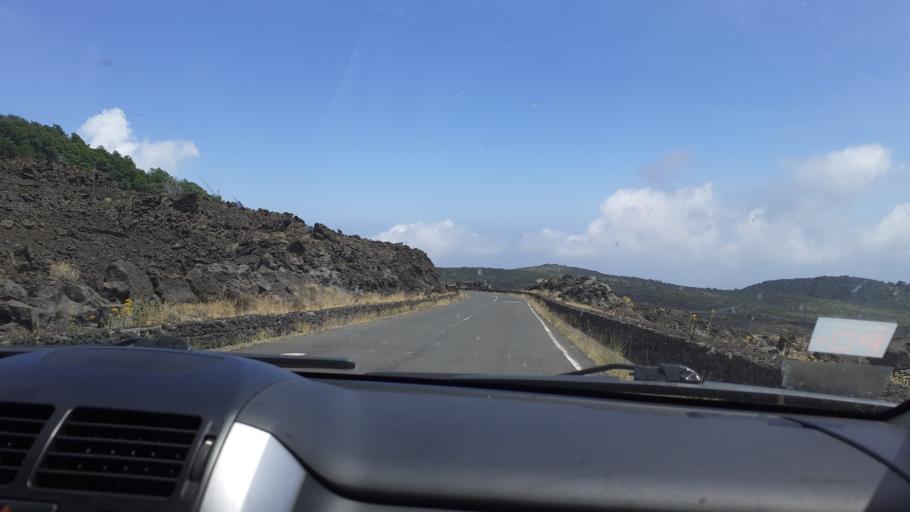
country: IT
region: Sicily
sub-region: Catania
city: Nicolosi
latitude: 37.6859
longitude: 15.0200
